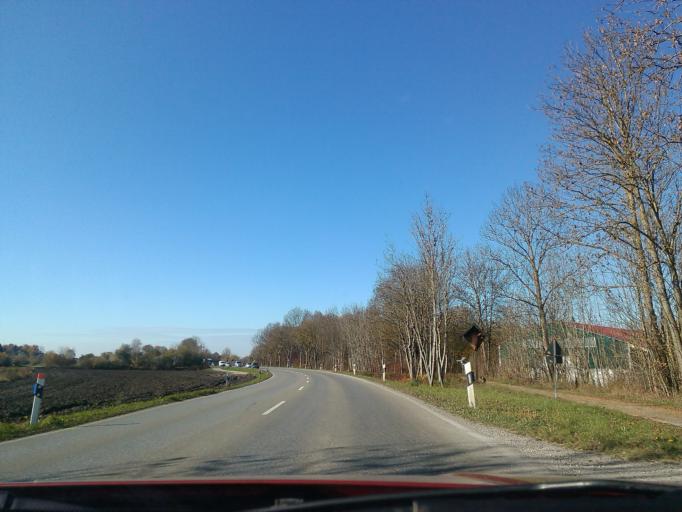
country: DE
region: Bavaria
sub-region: Upper Bavaria
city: Grobenzell
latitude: 48.1975
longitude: 11.3539
